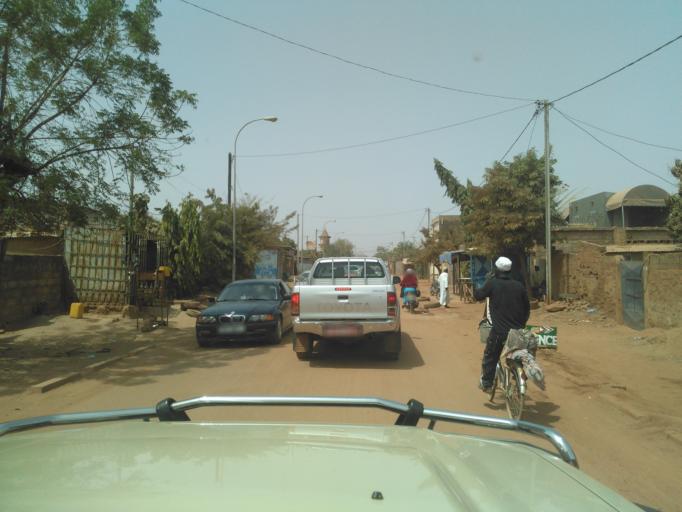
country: BF
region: Centre
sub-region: Kadiogo Province
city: Ouagadougou
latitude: 12.3944
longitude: -1.5509
